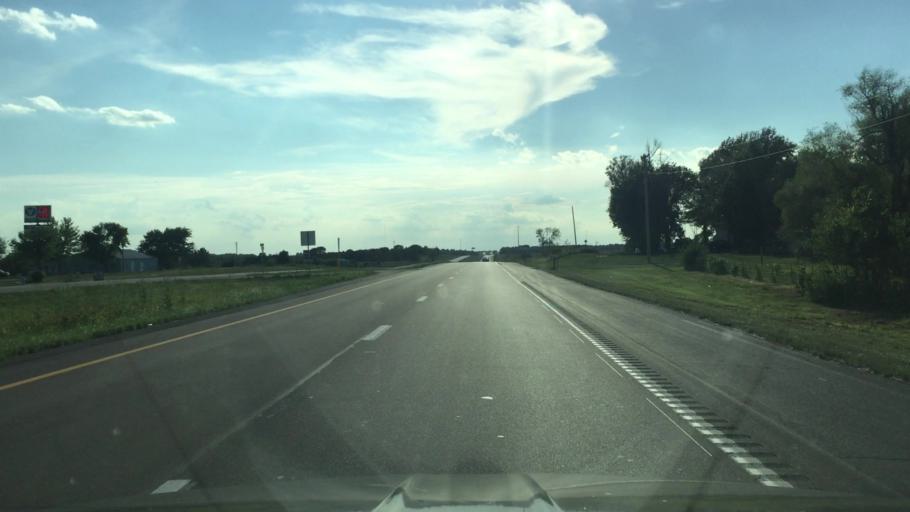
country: US
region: Missouri
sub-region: Pettis County
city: La Monte
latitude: 38.7618
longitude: -93.3806
